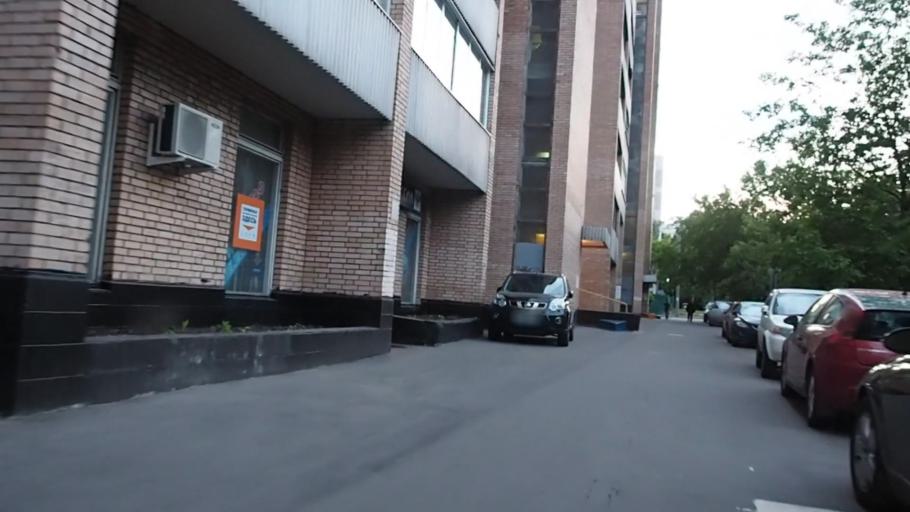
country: RU
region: Moscow
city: Sokol'niki
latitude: 55.7871
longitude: 37.6872
